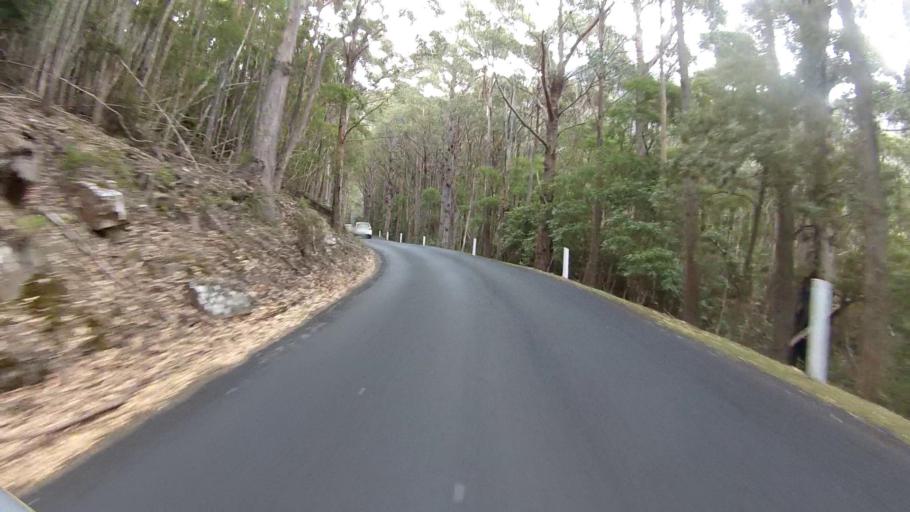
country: AU
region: Tasmania
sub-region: Hobart
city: Dynnyrne
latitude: -42.9124
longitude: 147.2541
